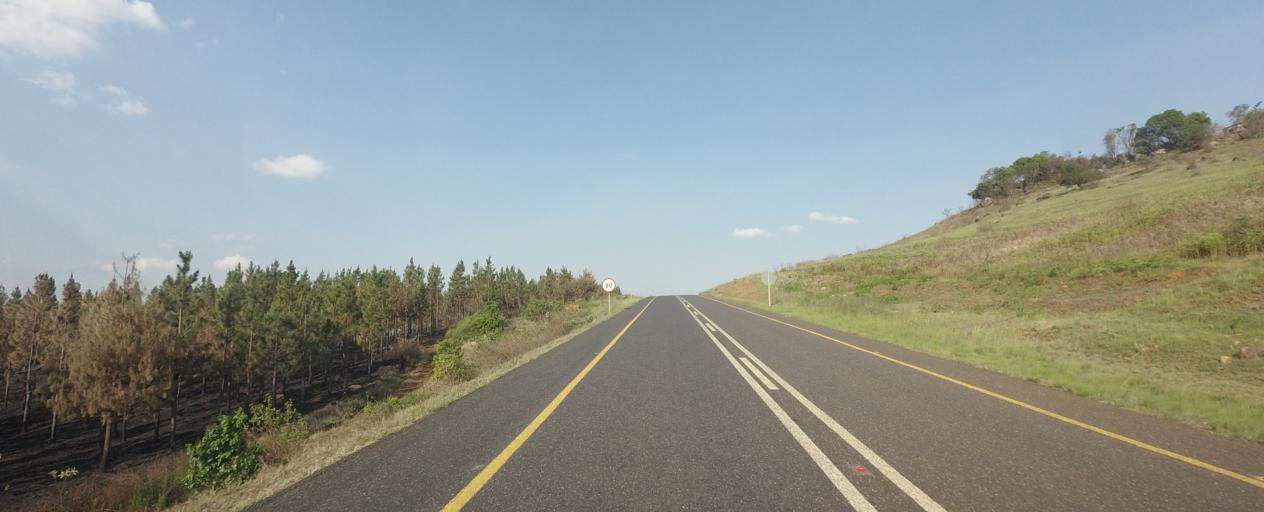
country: ZA
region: Mpumalanga
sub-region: Ehlanzeni District
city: Lydenburg
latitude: -25.1638
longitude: 30.6771
